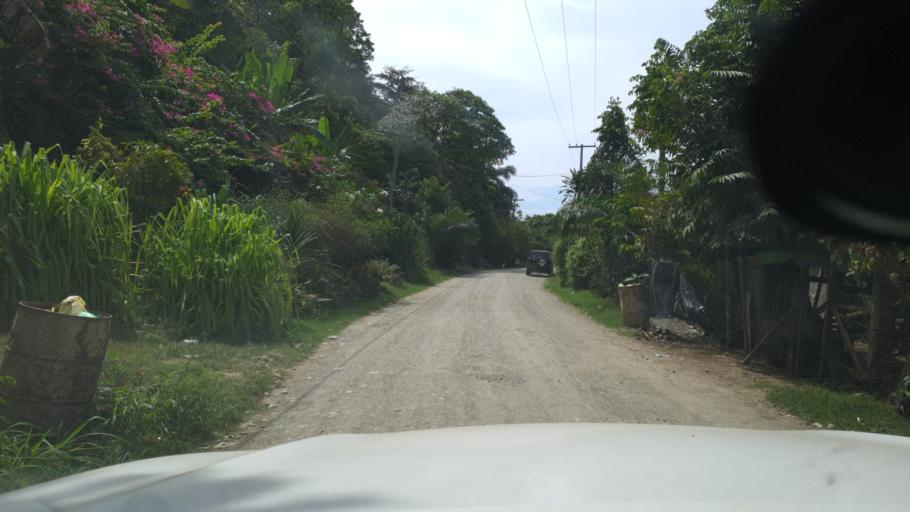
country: SB
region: Guadalcanal
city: Honiara
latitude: -9.4263
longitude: 159.9209
